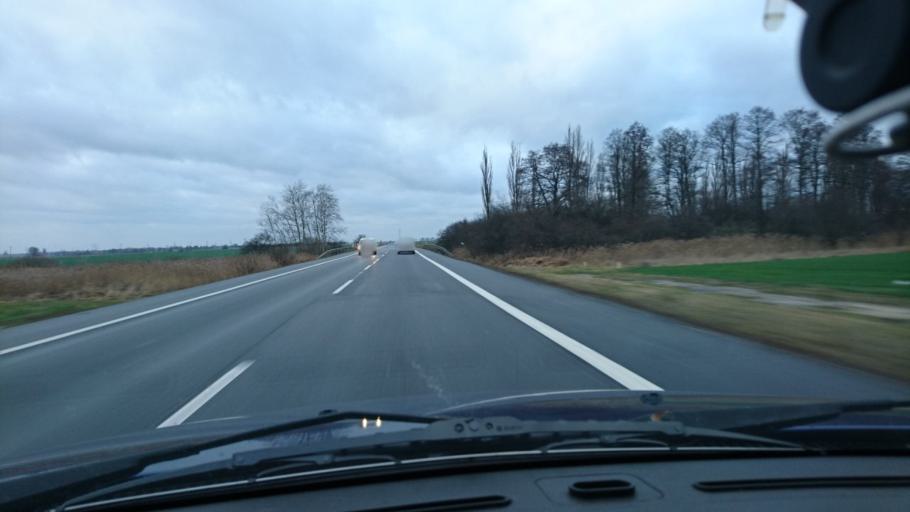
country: PL
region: Opole Voivodeship
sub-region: Powiat kluczborski
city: Kluczbork
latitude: 50.9845
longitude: 18.2413
